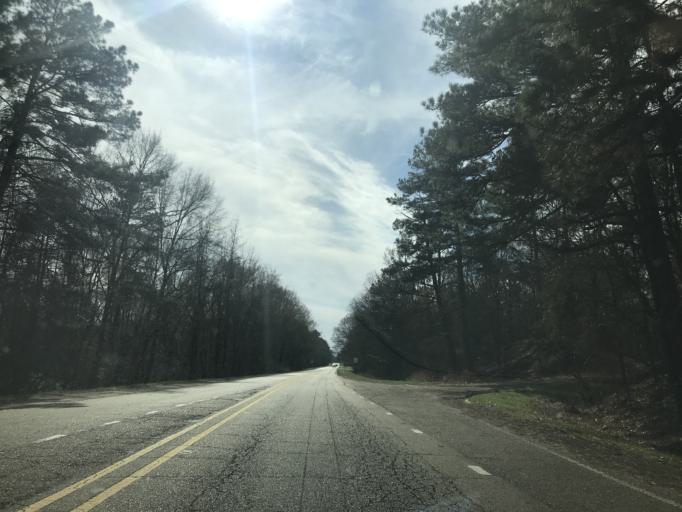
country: US
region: Mississippi
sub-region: Hinds County
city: Edwards
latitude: 32.1109
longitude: -90.6073
